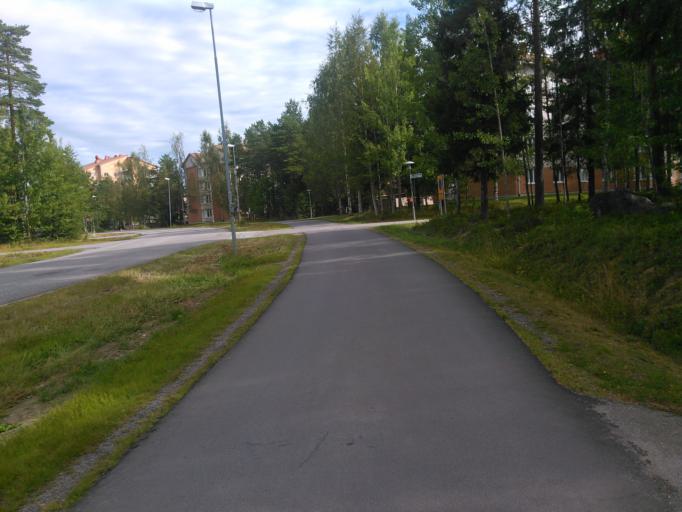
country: SE
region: Vaesterbotten
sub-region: Umea Kommun
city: Ersmark
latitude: 63.8243
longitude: 20.3259
